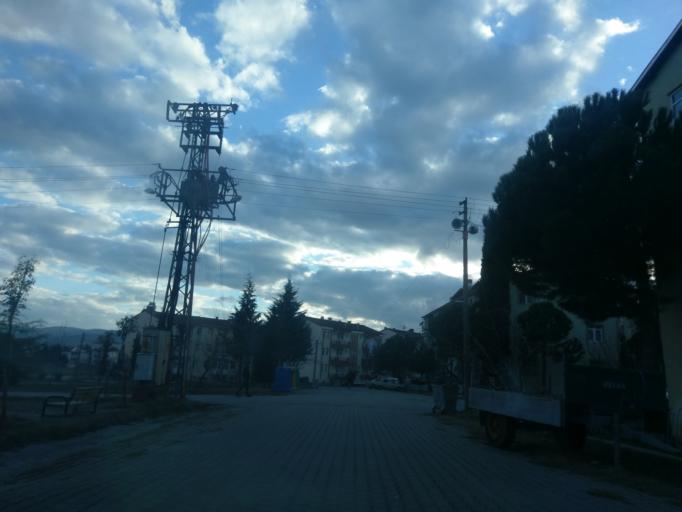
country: TR
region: Kuetahya
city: Gediz
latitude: 38.9942
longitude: 29.3852
